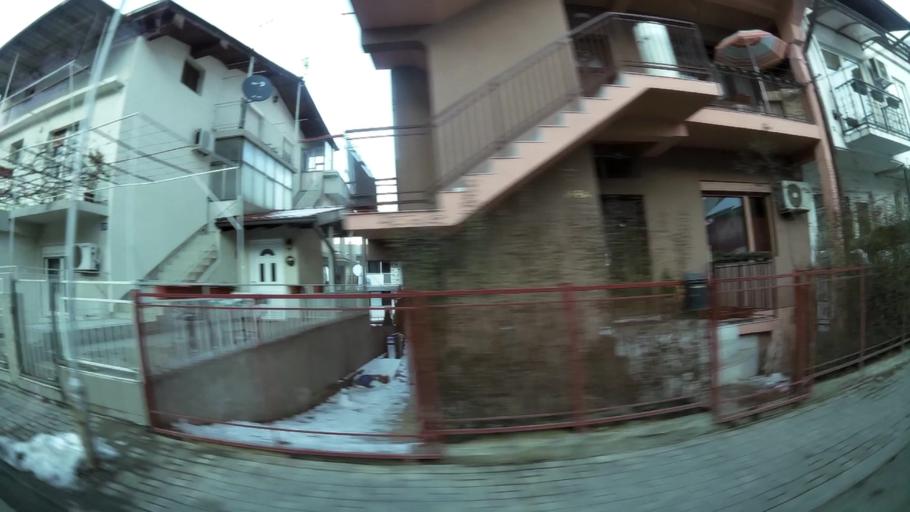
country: MK
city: Krushopek
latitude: 41.9972
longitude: 21.3853
